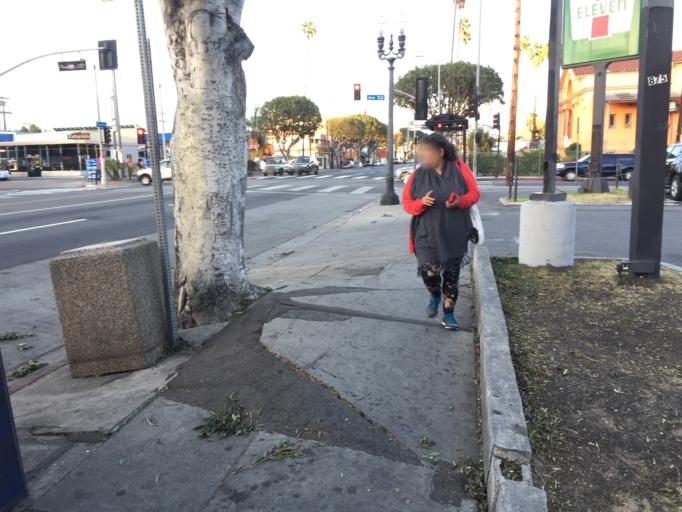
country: US
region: California
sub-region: Los Angeles County
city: South Pasadena
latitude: 34.1060
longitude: -118.1998
